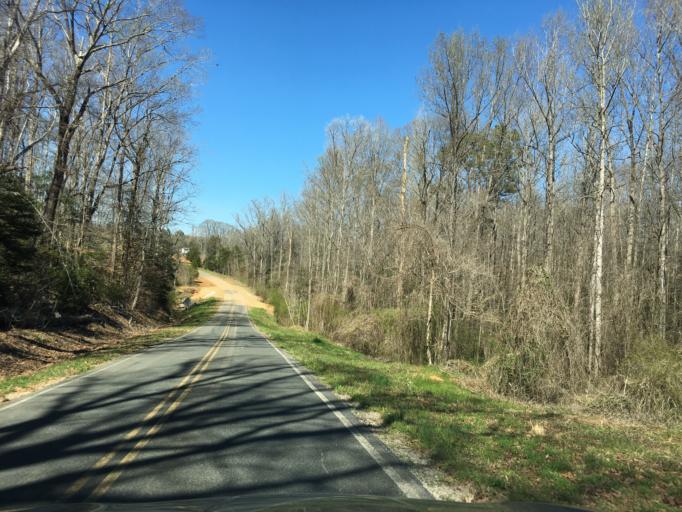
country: US
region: South Carolina
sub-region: Spartanburg County
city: Woodruff
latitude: 34.8201
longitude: -82.0795
